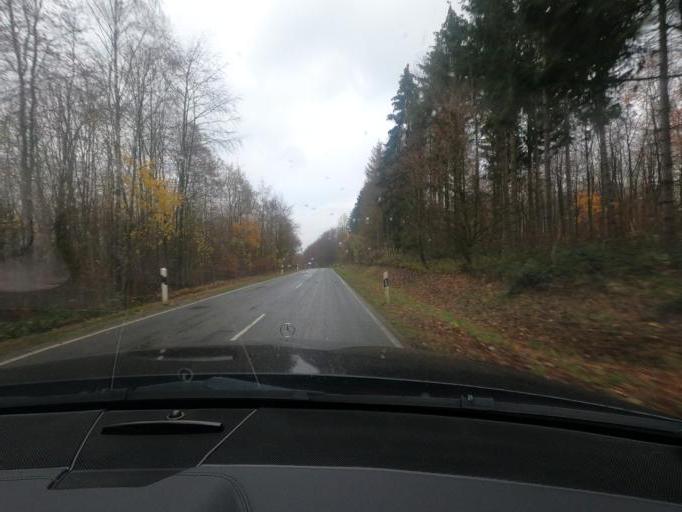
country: DE
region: North Rhine-Westphalia
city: Marsberg
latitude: 51.5490
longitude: 8.8128
